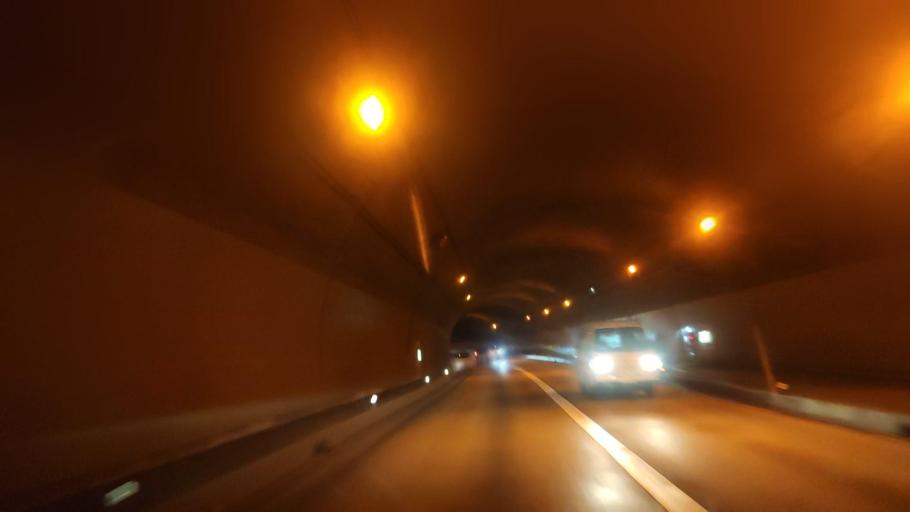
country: JP
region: Nagano
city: Okaya
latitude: 36.0891
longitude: 138.0611
